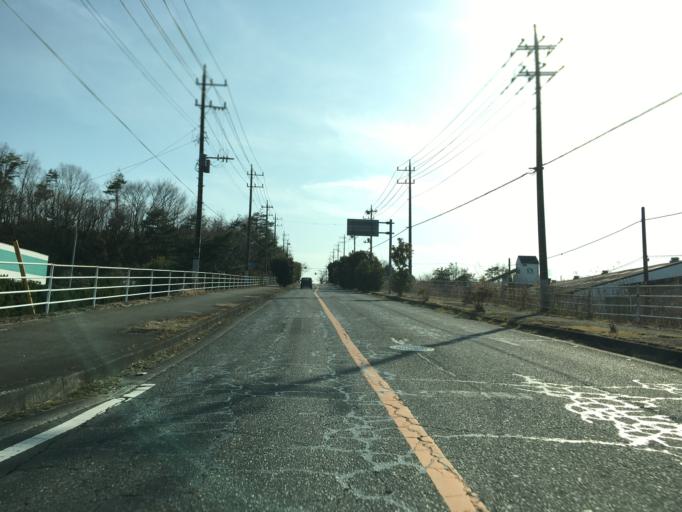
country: JP
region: Ibaraki
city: Takahagi
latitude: 36.7541
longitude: 140.7072
